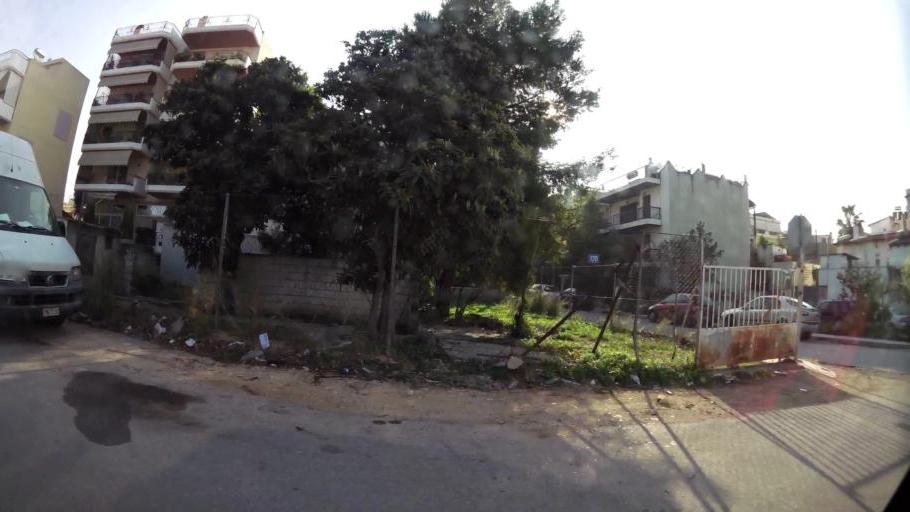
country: GR
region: Attica
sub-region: Nomarchia Dytikis Attikis
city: Zefyri
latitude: 38.0616
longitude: 23.7351
